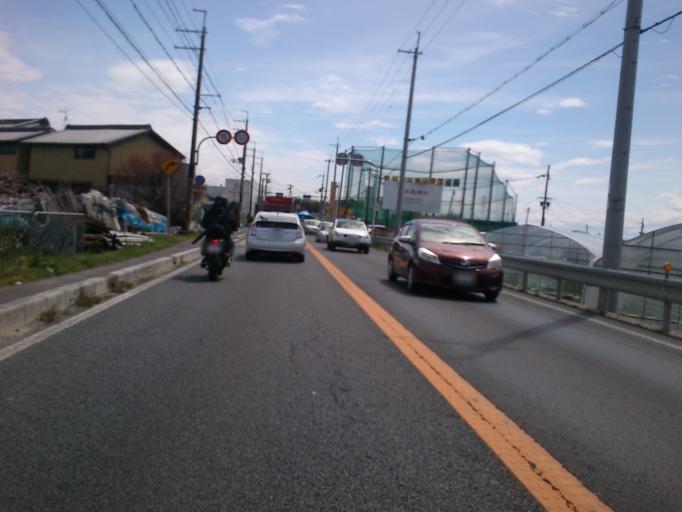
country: JP
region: Kyoto
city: Tanabe
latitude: 34.8370
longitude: 135.7910
